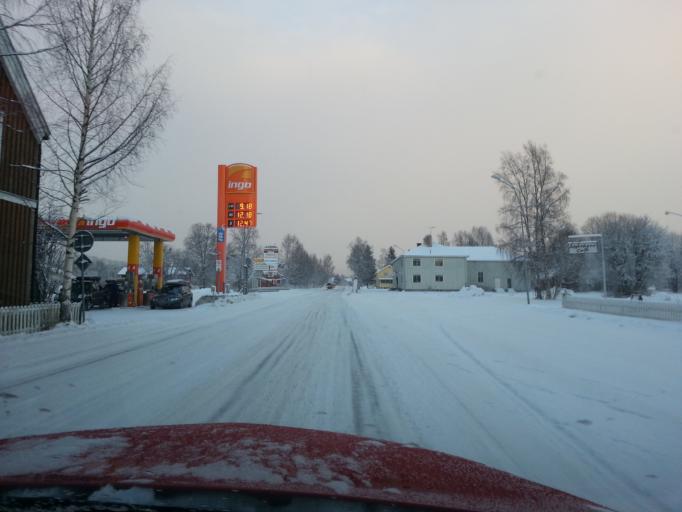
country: SE
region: Jaemtland
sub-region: Harjedalens Kommun
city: Sveg
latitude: 62.4483
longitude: 13.8630
